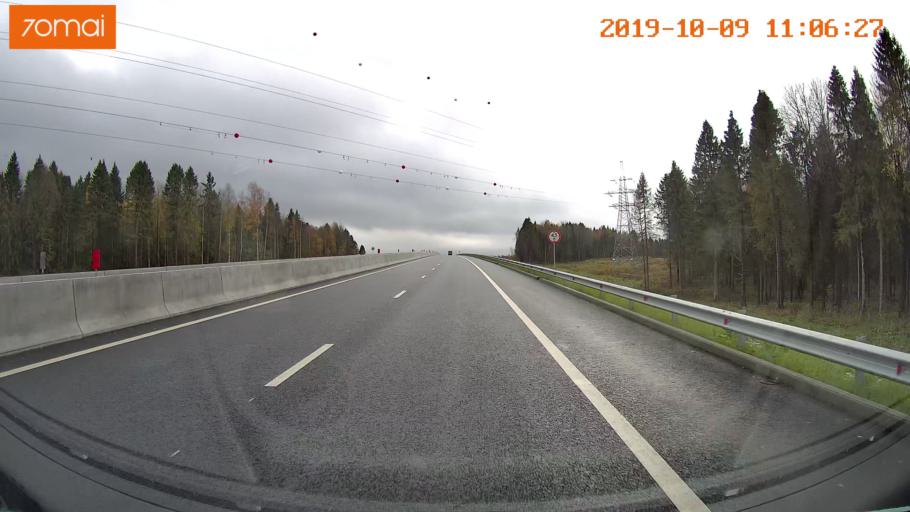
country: RU
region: Vologda
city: Vologda
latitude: 59.1862
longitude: 39.7607
